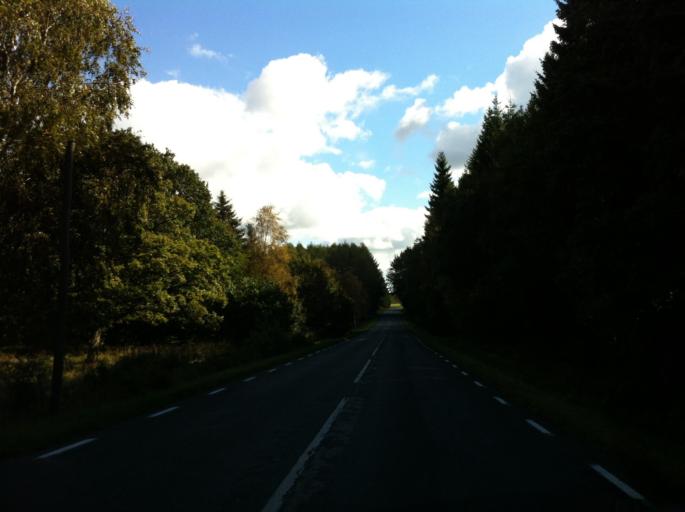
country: SE
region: Skane
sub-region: Kristianstads Kommun
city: Degeberga
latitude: 55.7702
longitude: 13.9012
